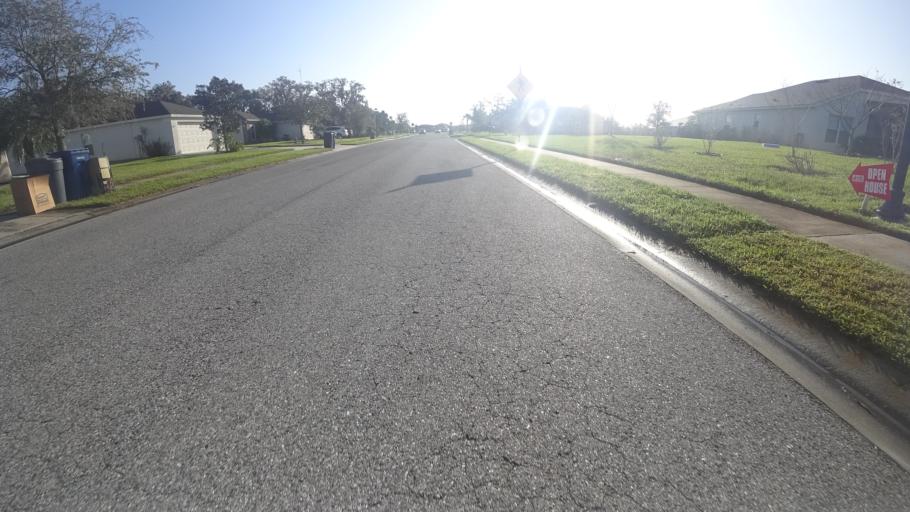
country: US
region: Florida
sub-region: Manatee County
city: Ellenton
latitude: 27.5687
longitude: -82.4545
